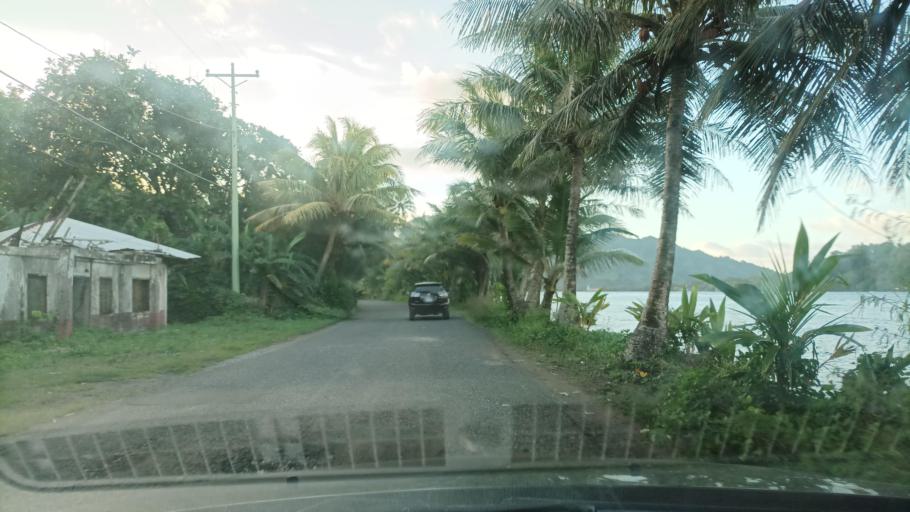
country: FM
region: Kosrae
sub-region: Lelu Municipality
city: Lelu
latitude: 5.3206
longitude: 163.0317
